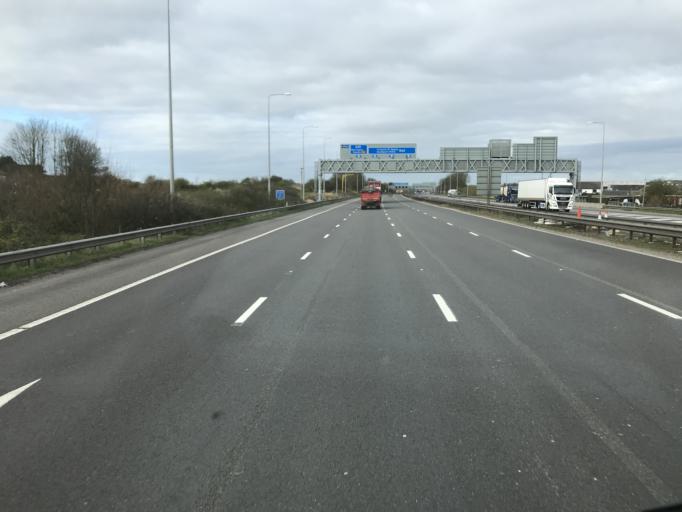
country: GB
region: England
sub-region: Warrington
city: Croft
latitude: 53.4240
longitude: -2.5691
